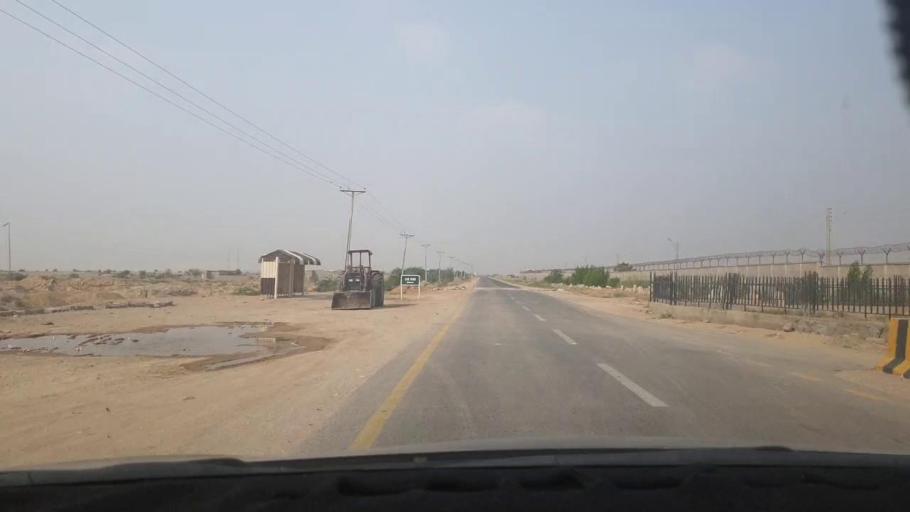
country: PK
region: Sindh
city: Jamshoro
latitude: 25.5606
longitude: 68.3185
